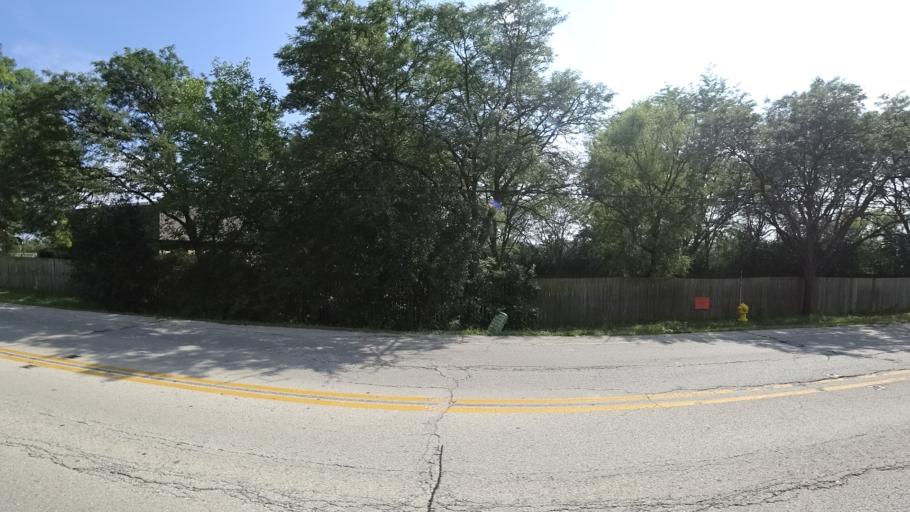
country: US
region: Illinois
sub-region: Cook County
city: Orland Park
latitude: 41.6516
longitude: -87.8923
